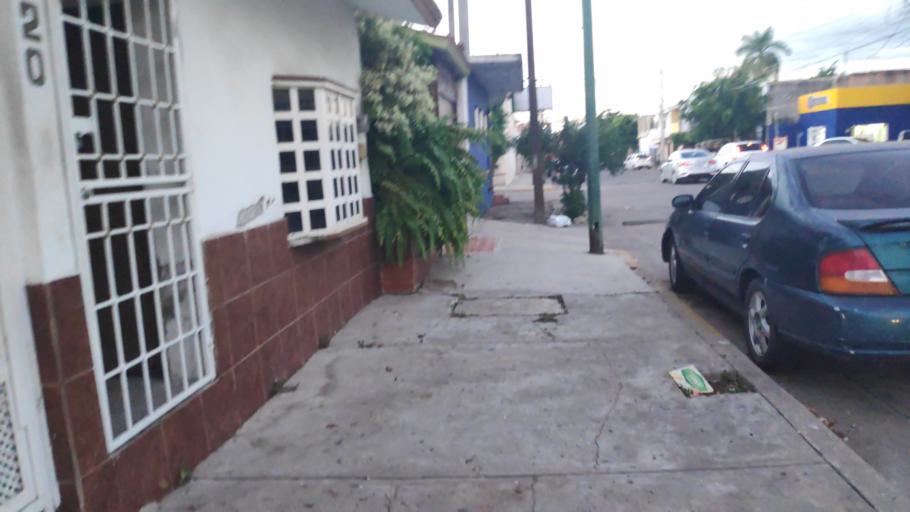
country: MX
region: Sinaloa
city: Culiacan
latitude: 24.7908
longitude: -107.4088
